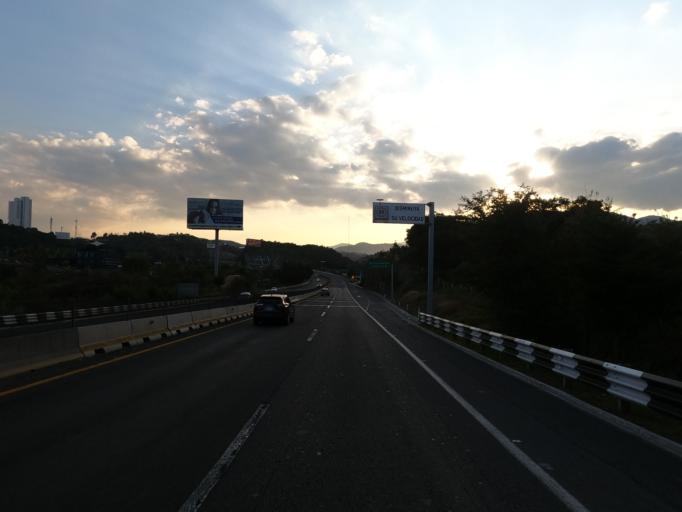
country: MX
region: Mexico
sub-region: Naucalpan de Juarez
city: Ejido el Castillo
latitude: 19.4236
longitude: -99.2971
